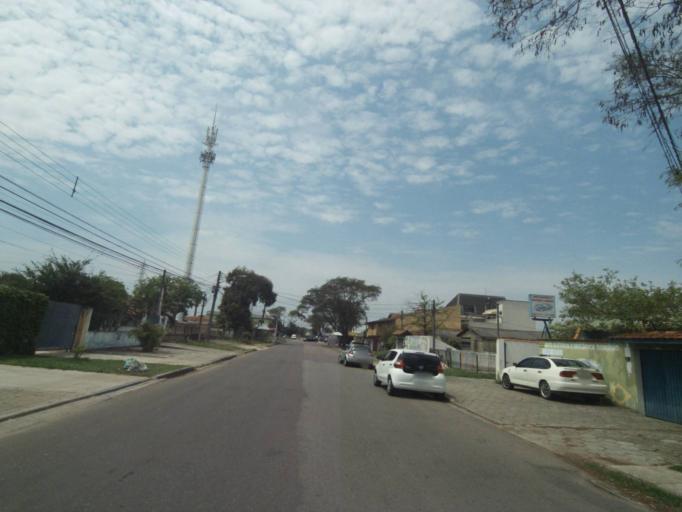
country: BR
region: Parana
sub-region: Pinhais
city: Pinhais
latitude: -25.4215
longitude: -49.1995
